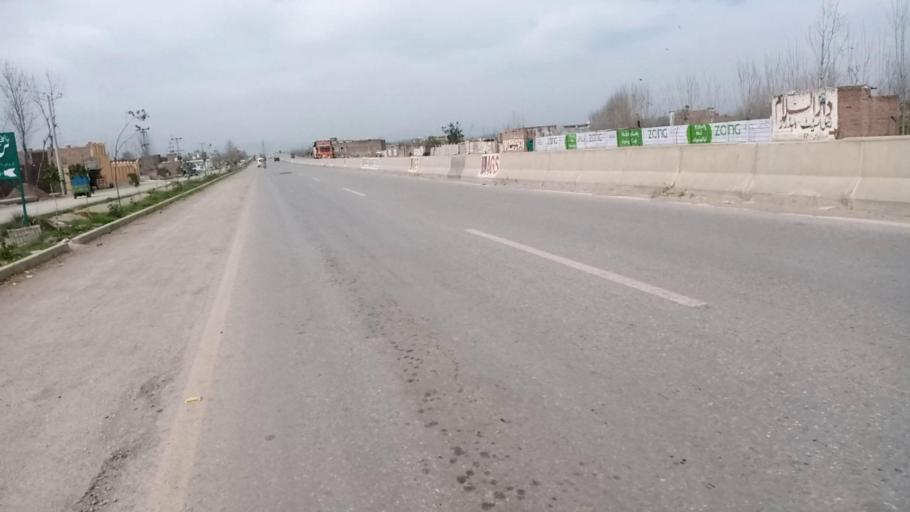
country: PK
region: Khyber Pakhtunkhwa
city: Peshawar
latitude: 34.0445
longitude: 71.6166
